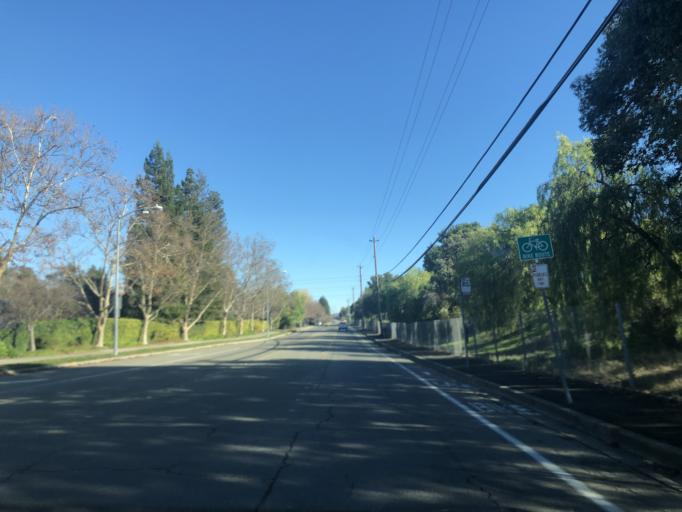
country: US
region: California
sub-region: Contra Costa County
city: Vine Hill
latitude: 37.9911
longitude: -122.0944
